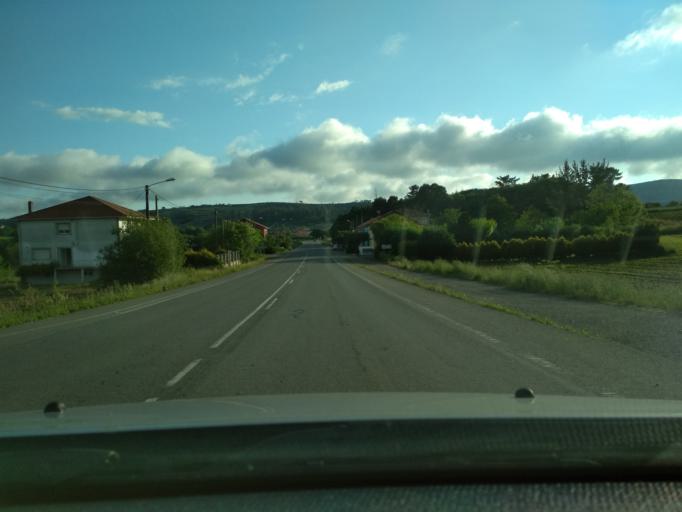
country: ES
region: Galicia
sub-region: Provincia da Coruna
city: Mazaricos
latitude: 42.9581
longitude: -8.9244
